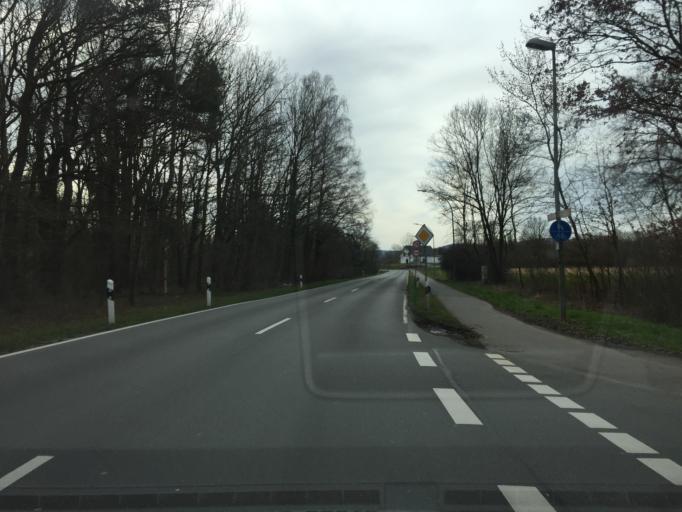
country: DE
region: North Rhine-Westphalia
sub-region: Regierungsbezirk Detmold
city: Lage
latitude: 51.9703
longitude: 8.8012
